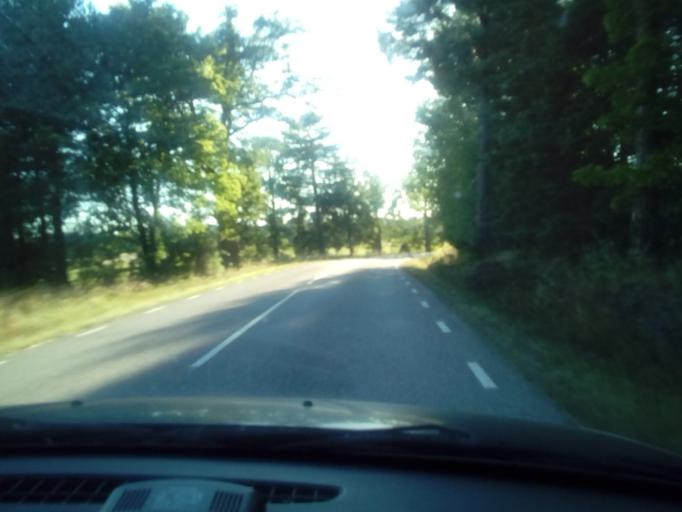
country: SE
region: Kalmar
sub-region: Vasterviks Kommun
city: Gamleby
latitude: 57.7876
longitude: 16.3936
